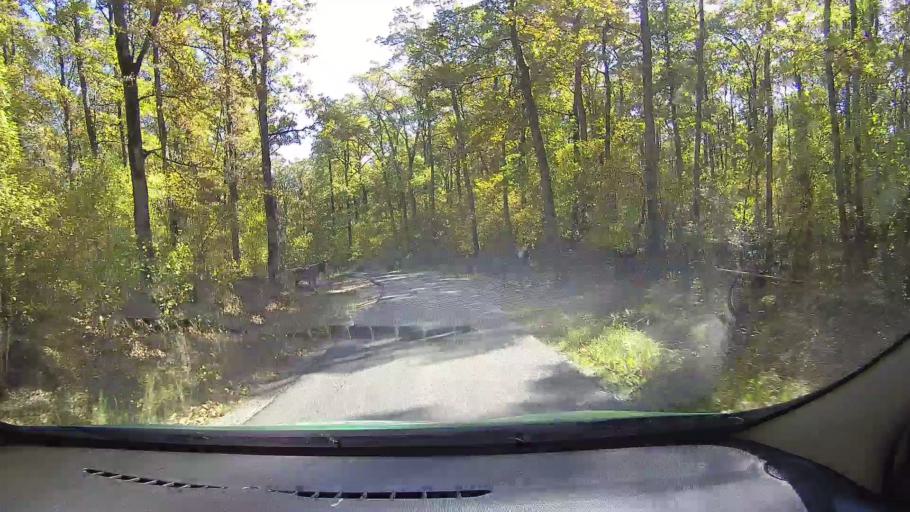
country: RO
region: Satu Mare
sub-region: Municipiul Satu Mare
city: Satmarel
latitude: 47.7045
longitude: 22.7687
